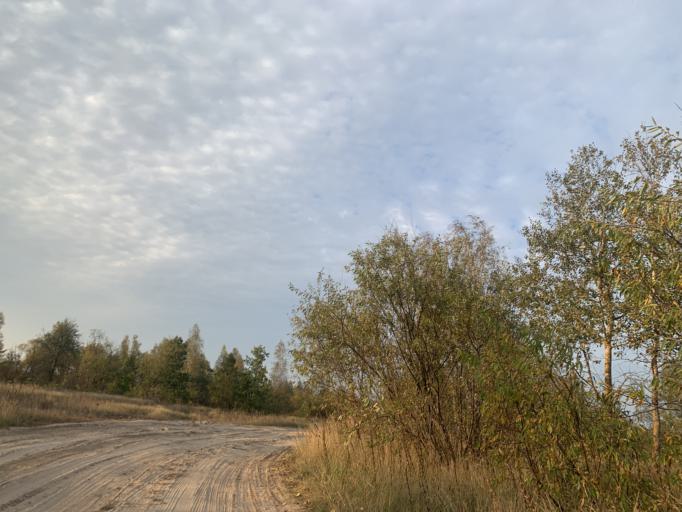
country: BY
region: Brest
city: Mikashevichy
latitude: 52.3312
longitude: 27.4972
